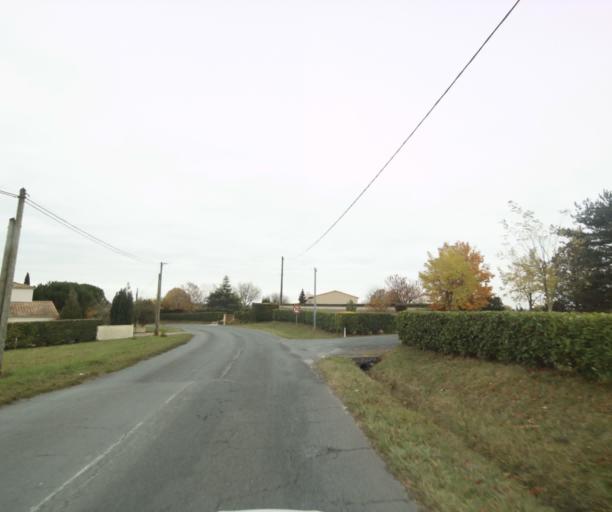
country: FR
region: Poitou-Charentes
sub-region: Departement de la Charente-Maritime
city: Les Gonds
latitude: 45.7219
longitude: -0.6337
